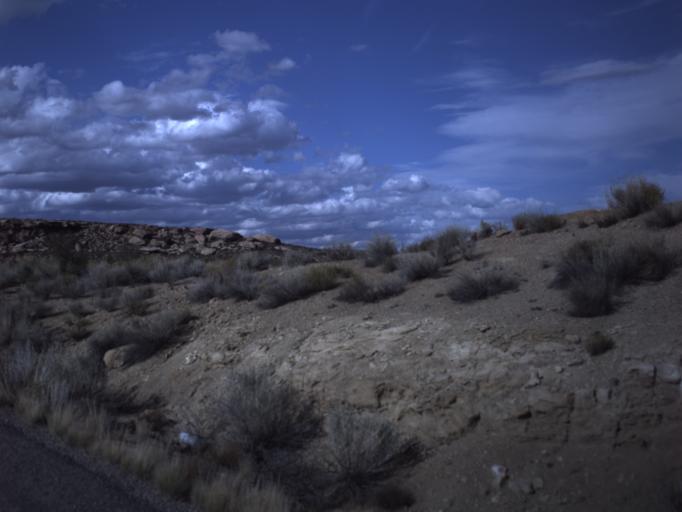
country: US
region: Utah
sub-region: San Juan County
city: Blanding
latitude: 37.3277
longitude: -109.3226
